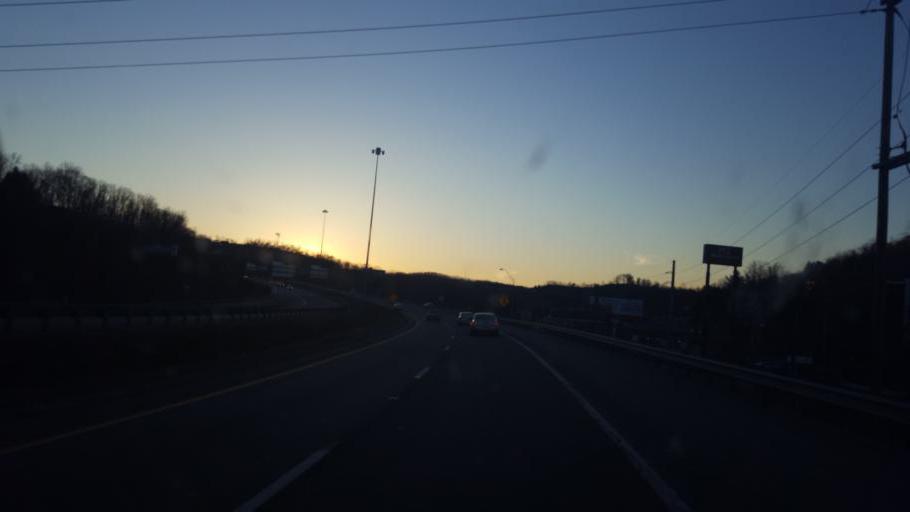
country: US
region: West Virginia
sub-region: Ohio County
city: Wheeling
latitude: 40.0743
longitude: -80.7028
